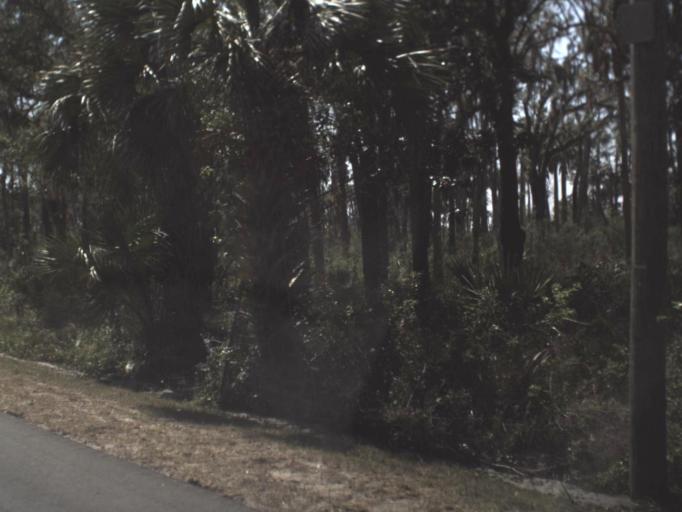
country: US
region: Florida
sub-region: Gulf County
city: Port Saint Joe
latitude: 29.7299
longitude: -85.3025
